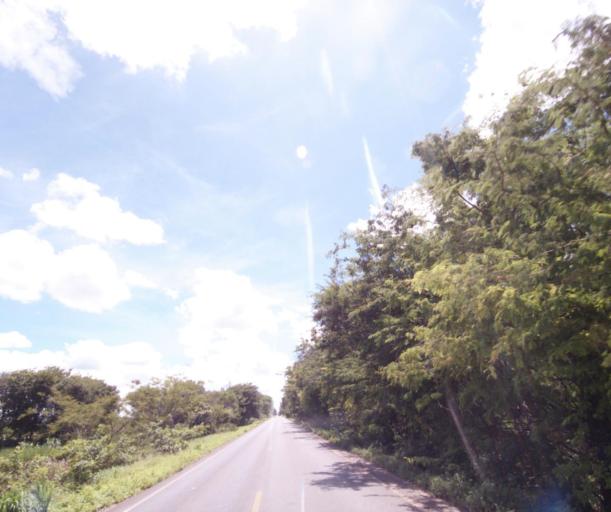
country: BR
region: Bahia
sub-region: Bom Jesus Da Lapa
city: Bom Jesus da Lapa
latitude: -13.2642
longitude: -43.5676
